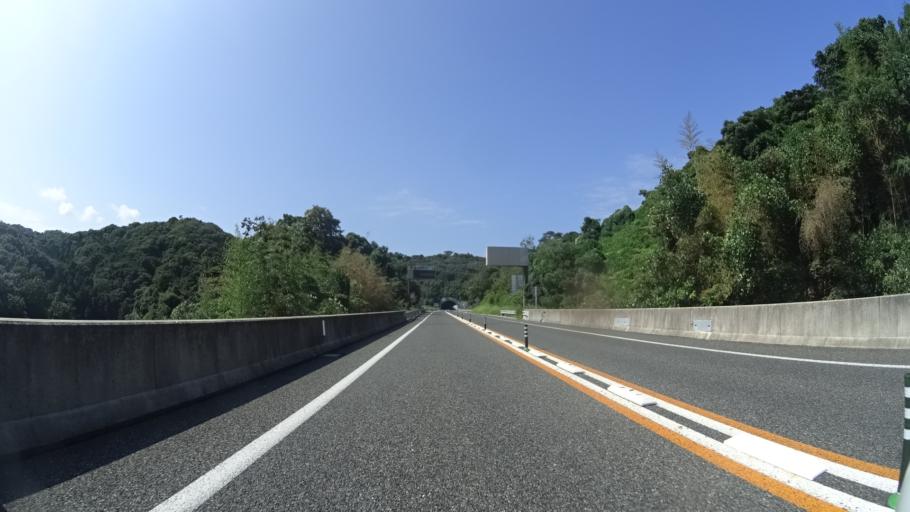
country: JP
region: Shimane
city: Gotsucho
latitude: 34.9671
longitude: 132.1688
